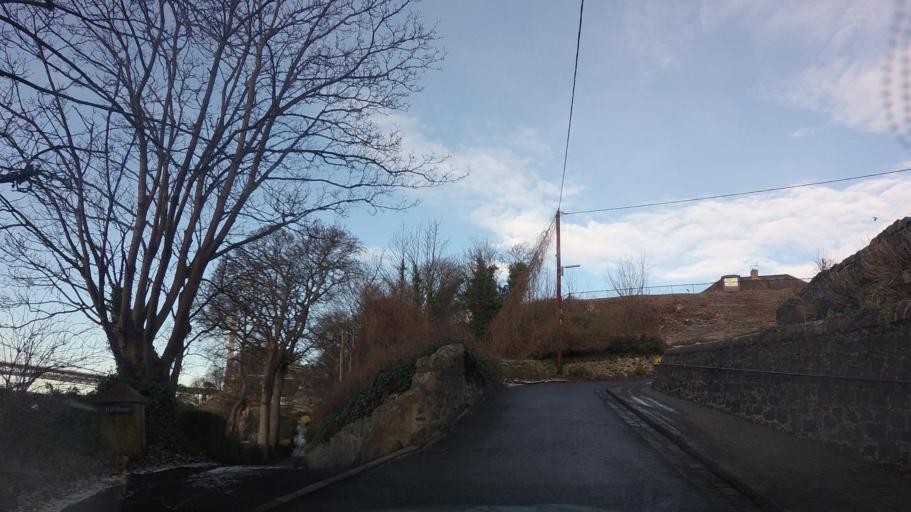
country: GB
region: Scotland
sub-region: Fife
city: North Queensferry
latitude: 56.0104
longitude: -3.3947
